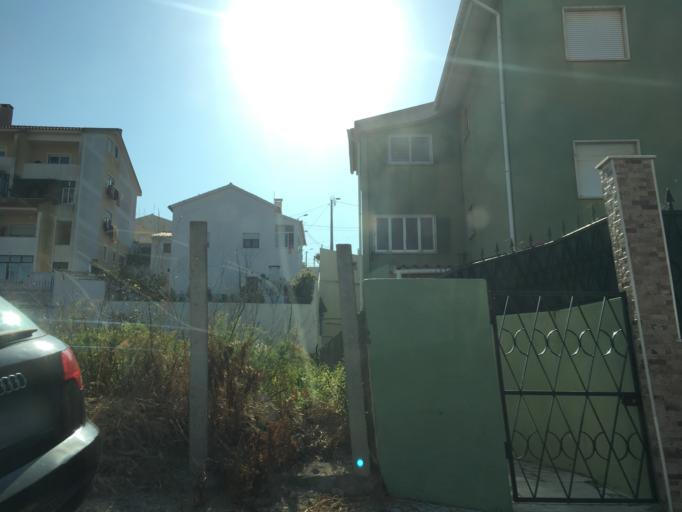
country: PT
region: Lisbon
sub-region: Cascais
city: Sao Domingos de Rana
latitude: 38.7100
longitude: -9.3449
